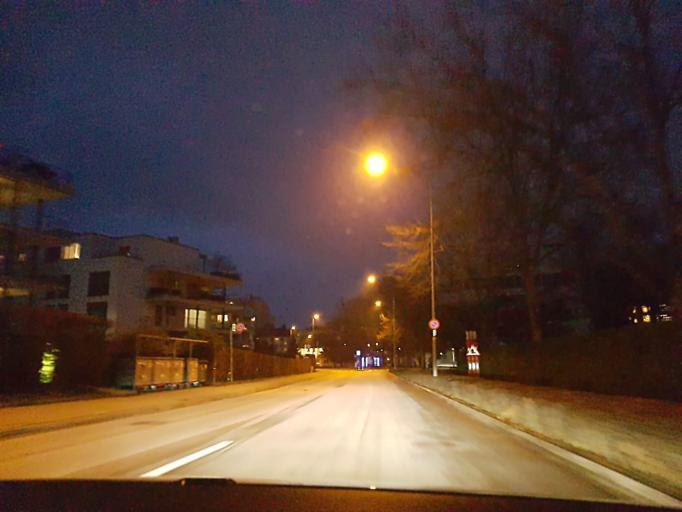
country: CH
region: Zurich
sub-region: Bezirk Horgen
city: Ruschlikon
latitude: 47.3078
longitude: 8.5472
